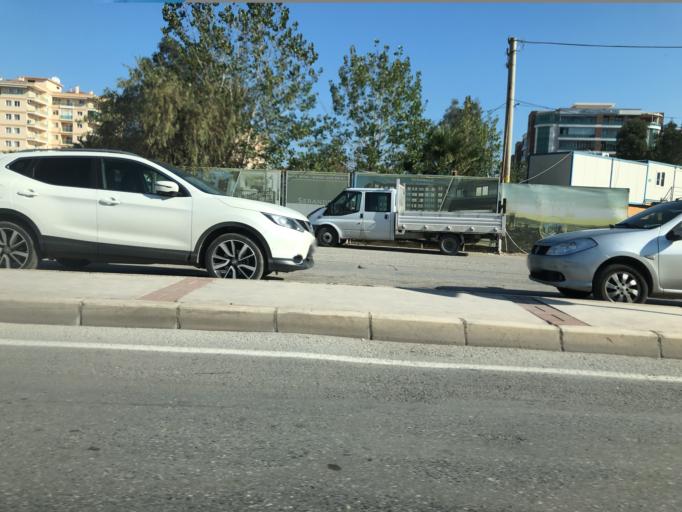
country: TR
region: Izmir
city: Izmir
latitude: 38.4596
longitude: 27.1742
